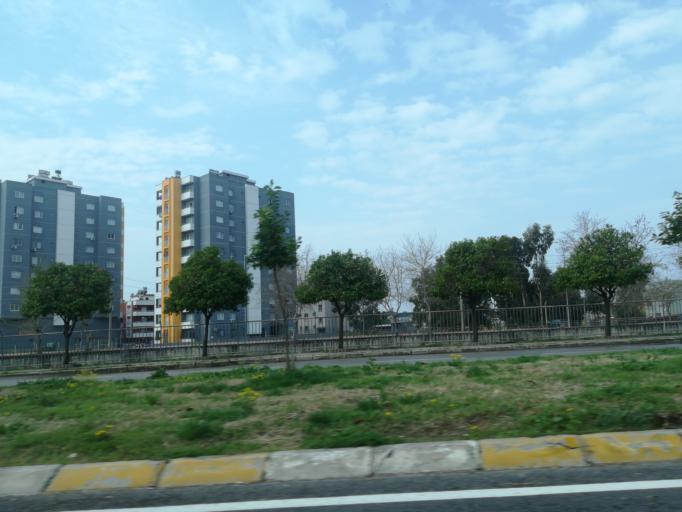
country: TR
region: Adana
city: Yuregir
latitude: 36.9900
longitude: 35.3637
